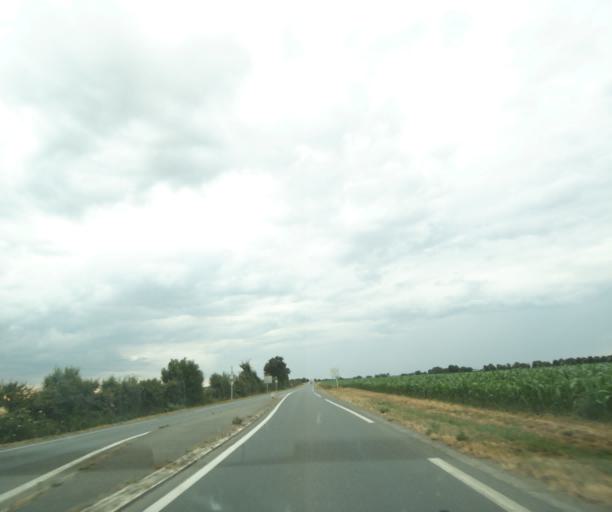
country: FR
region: Pays de la Loire
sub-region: Departement de la Vendee
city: Sainte-Gemme-la-Plaine
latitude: 46.4521
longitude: -1.1041
